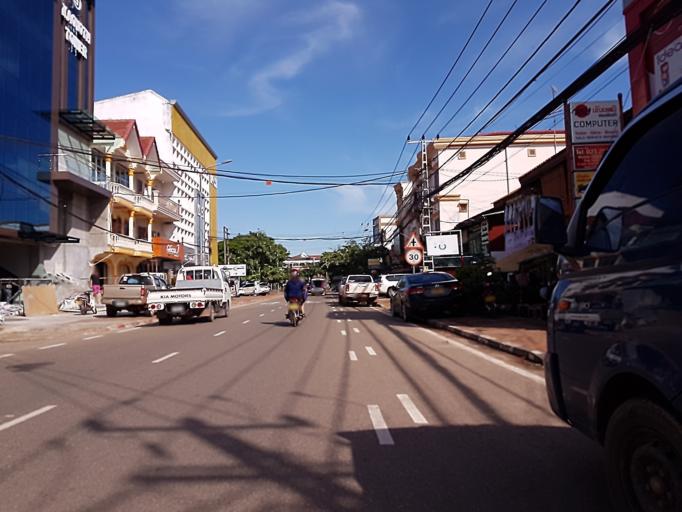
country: LA
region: Vientiane
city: Vientiane
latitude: 17.9602
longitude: 102.6167
